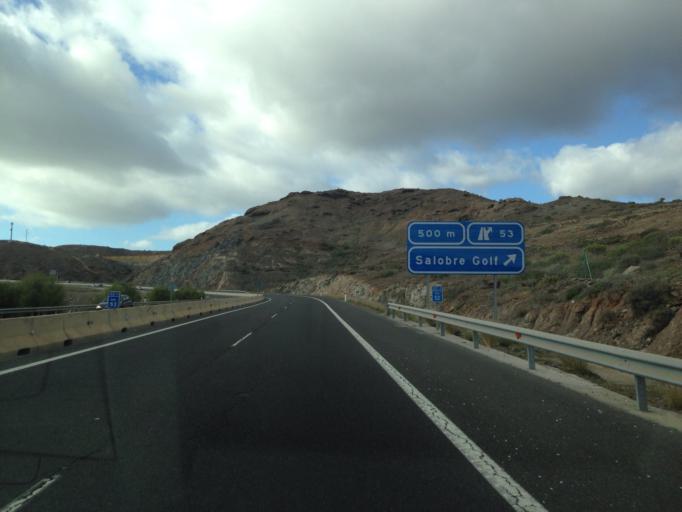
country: ES
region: Canary Islands
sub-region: Provincia de Las Palmas
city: Maspalomas
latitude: 27.7695
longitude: -15.6339
